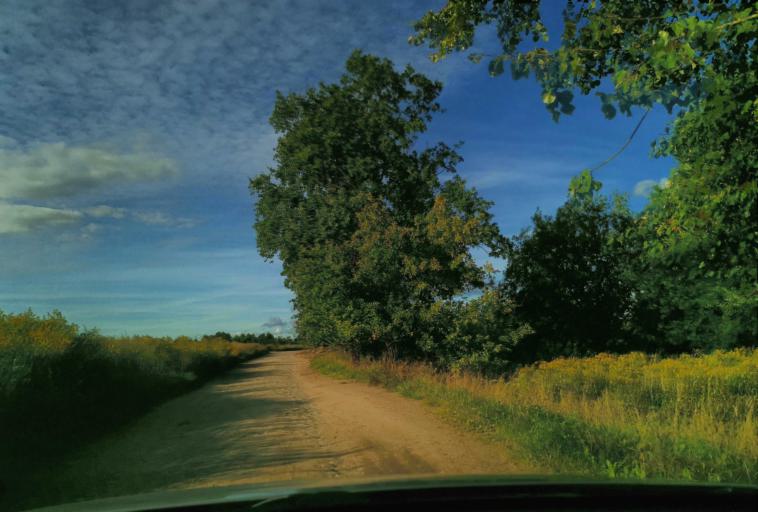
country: RU
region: Kaliningrad
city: Chernyakhovsk
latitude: 54.6355
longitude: 21.7662
